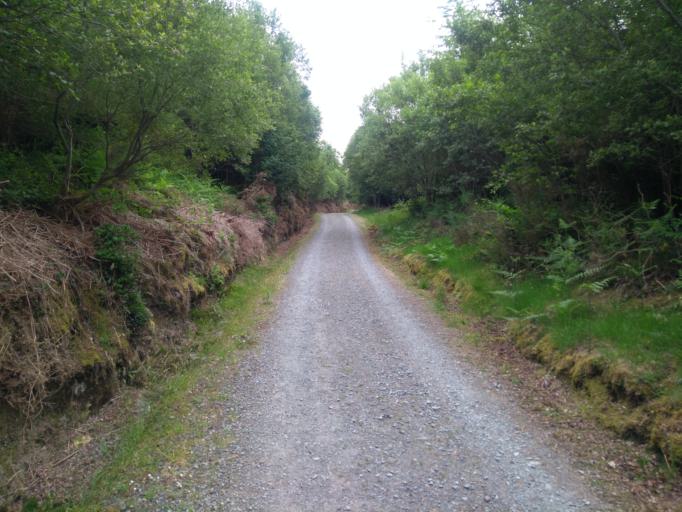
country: IE
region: Munster
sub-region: Ciarrai
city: Kenmare
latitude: 51.8313
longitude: -9.5174
